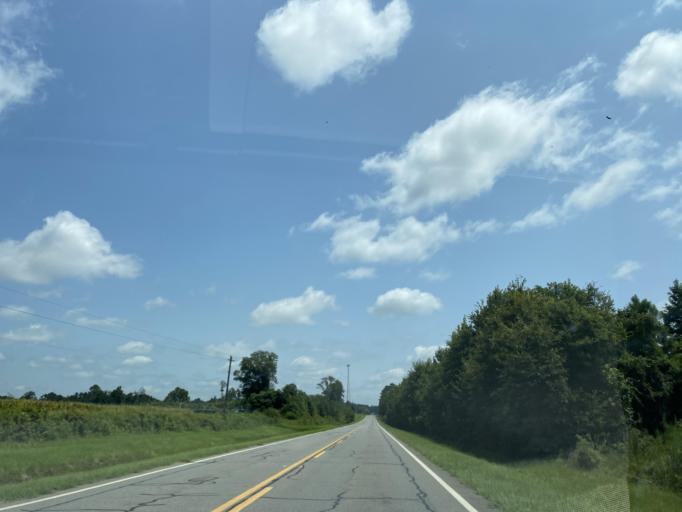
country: US
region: Georgia
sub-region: Wilcox County
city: Abbeville
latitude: 31.9969
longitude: -83.1832
